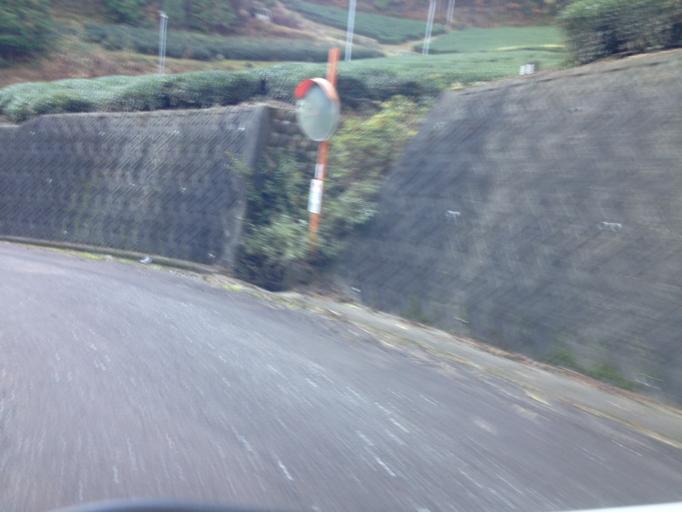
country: JP
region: Gifu
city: Mitake
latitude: 35.6104
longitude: 137.2039
